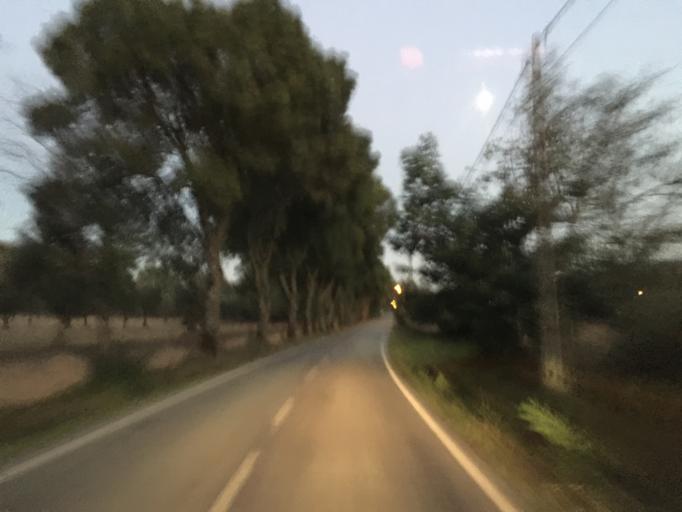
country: PT
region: Portalegre
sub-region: Marvao
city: Marvao
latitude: 39.3932
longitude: -7.4164
